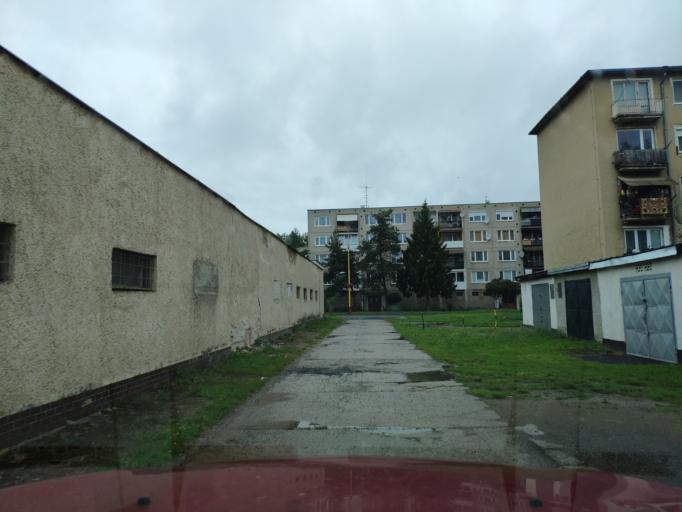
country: SK
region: Kosicky
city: Cierna nad Tisou
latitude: 48.4163
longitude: 22.0844
